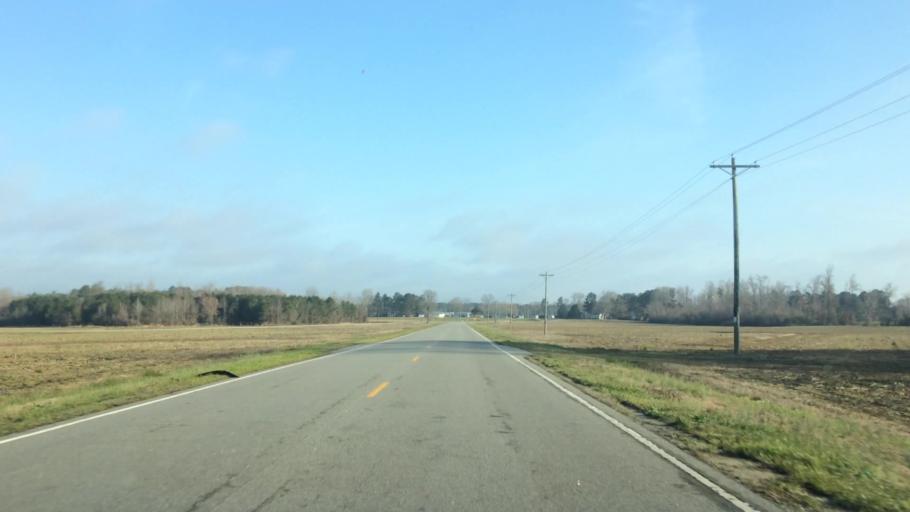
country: US
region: North Carolina
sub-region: Edgecombe County
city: Pinetops
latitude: 35.7233
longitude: -77.6349
